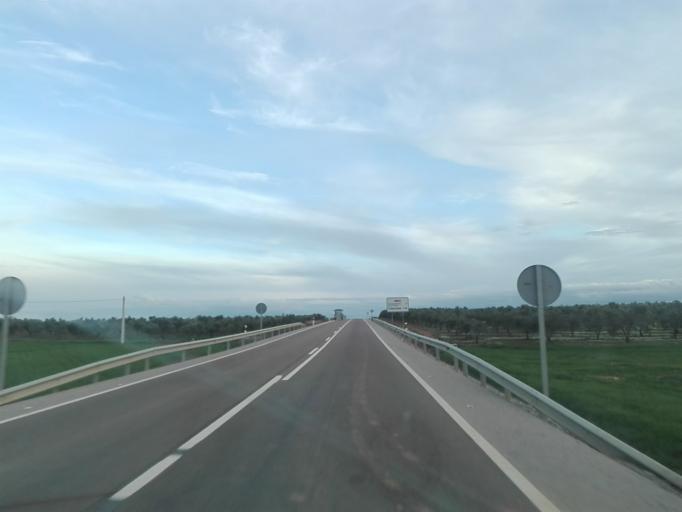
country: ES
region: Extremadura
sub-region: Provincia de Badajoz
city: Usagre
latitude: 38.3428
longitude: -6.1669
